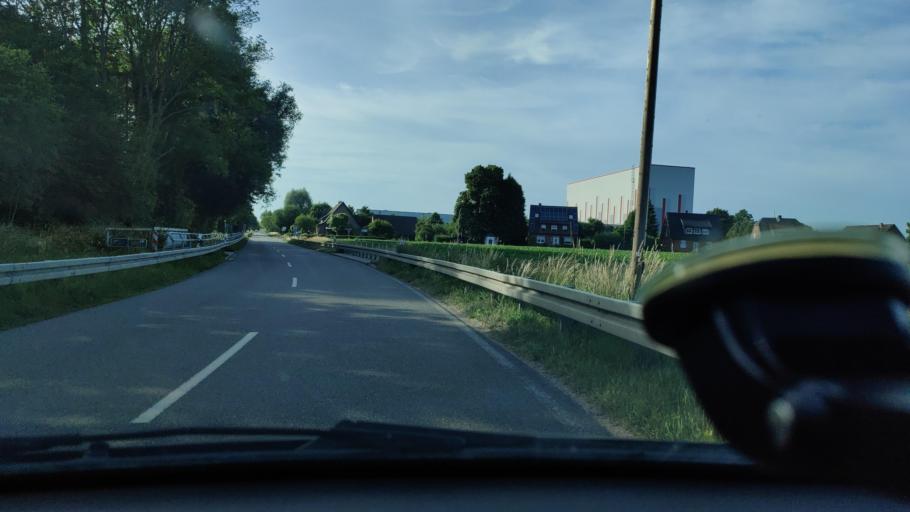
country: DE
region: North Rhine-Westphalia
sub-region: Regierungsbezirk Munster
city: Coesfeld
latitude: 52.0101
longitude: 7.1912
